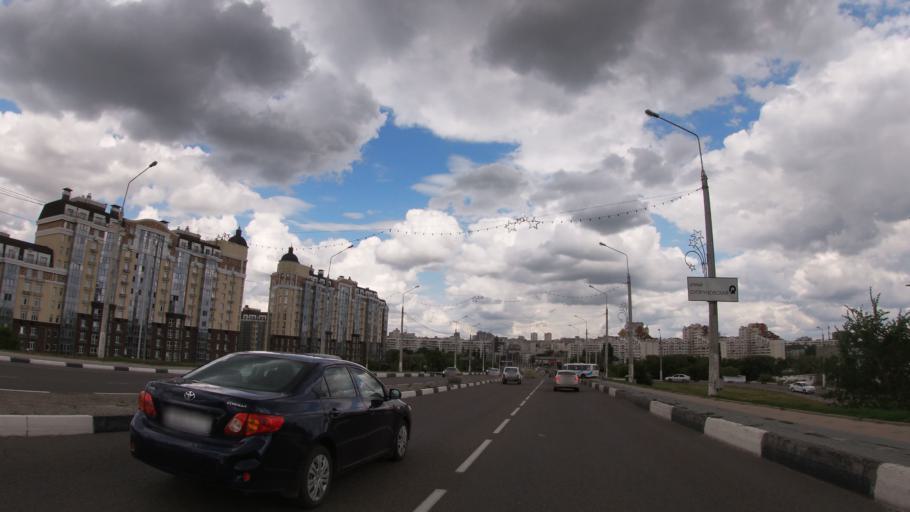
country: RU
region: Belgorod
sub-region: Belgorodskiy Rayon
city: Belgorod
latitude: 50.5875
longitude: 36.5883
